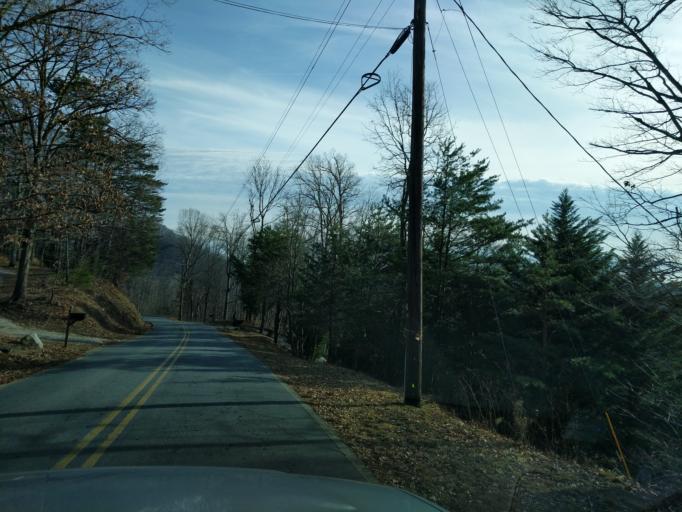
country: US
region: North Carolina
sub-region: Polk County
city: Columbus
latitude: 35.2664
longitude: -82.2092
